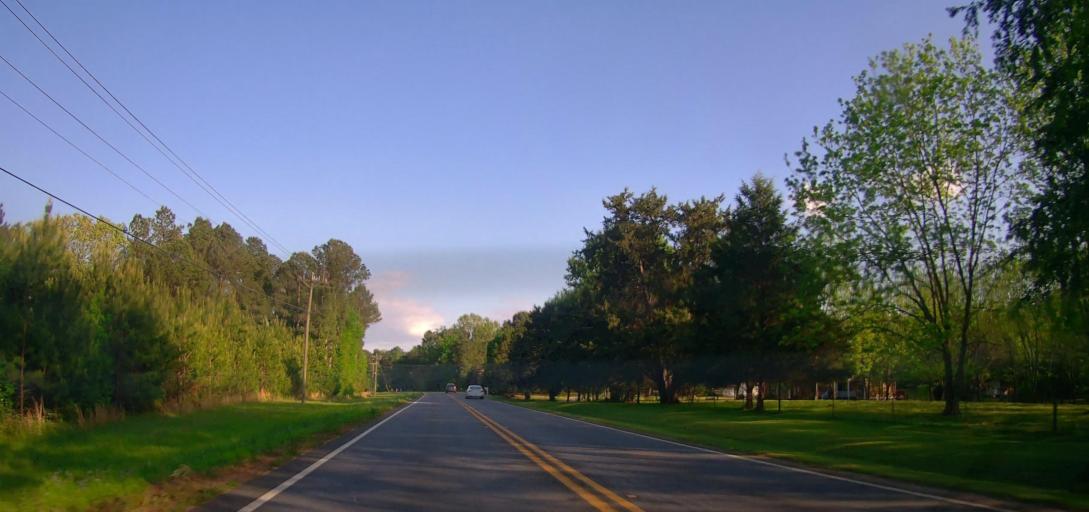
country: US
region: Georgia
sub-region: Putnam County
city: Eatonton
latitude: 33.3137
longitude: -83.4923
